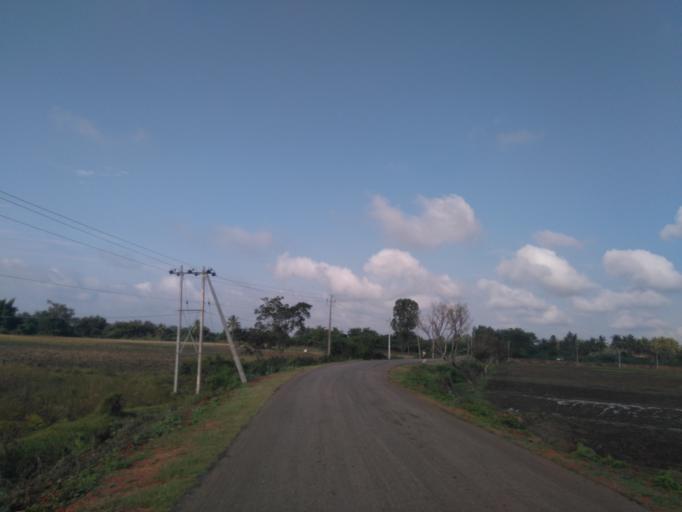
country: IN
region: Karnataka
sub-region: Mysore
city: Tirumakudal Narsipur
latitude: 12.2573
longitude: 76.9922
